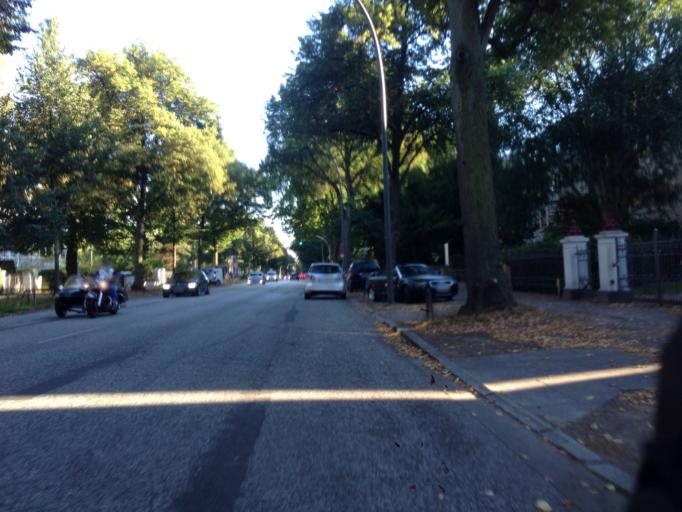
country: DE
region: Hamburg
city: Eimsbuettel
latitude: 53.5753
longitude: 9.9887
